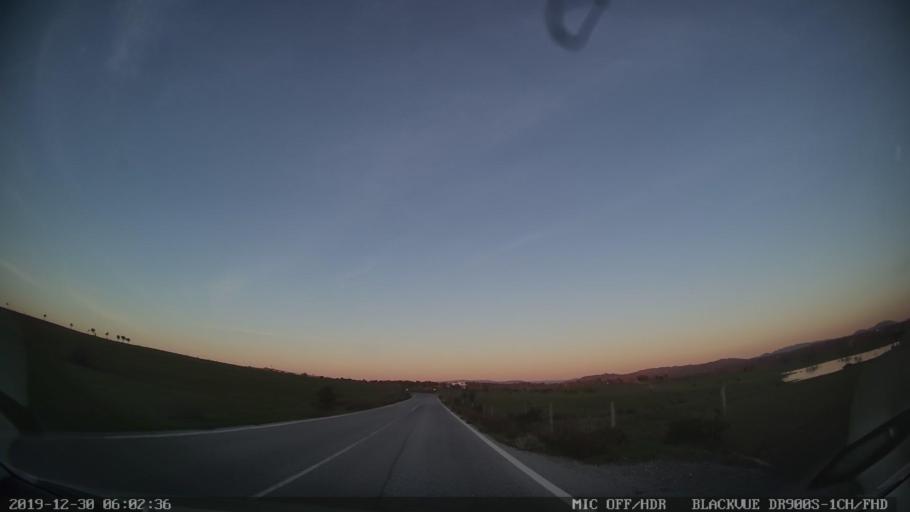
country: PT
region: Castelo Branco
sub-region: Penamacor
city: Penamacor
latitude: 40.0715
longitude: -7.2427
